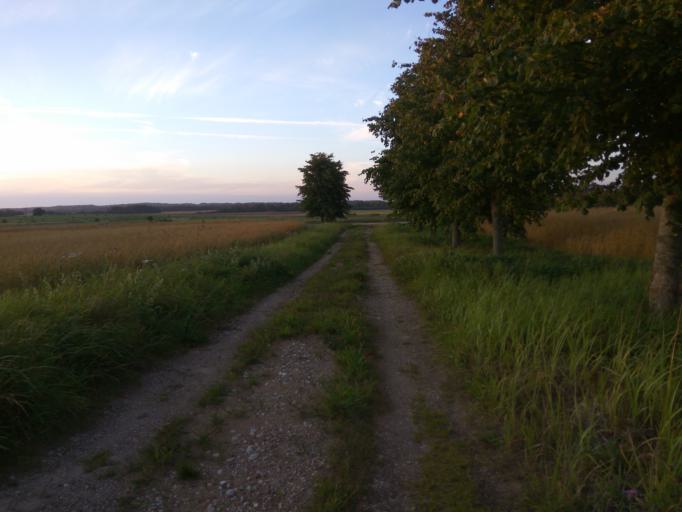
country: LV
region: Aizpute
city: Aizpute
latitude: 56.8376
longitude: 21.7382
